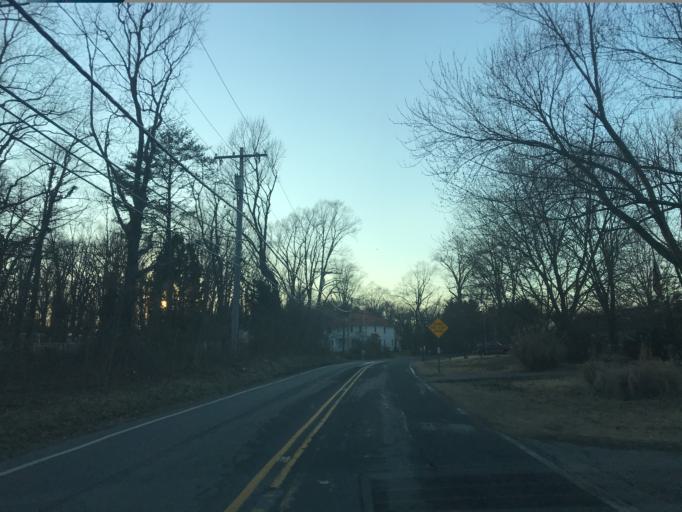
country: US
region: Maryland
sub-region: Anne Arundel County
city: Arnold
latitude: 39.0352
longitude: -76.4913
